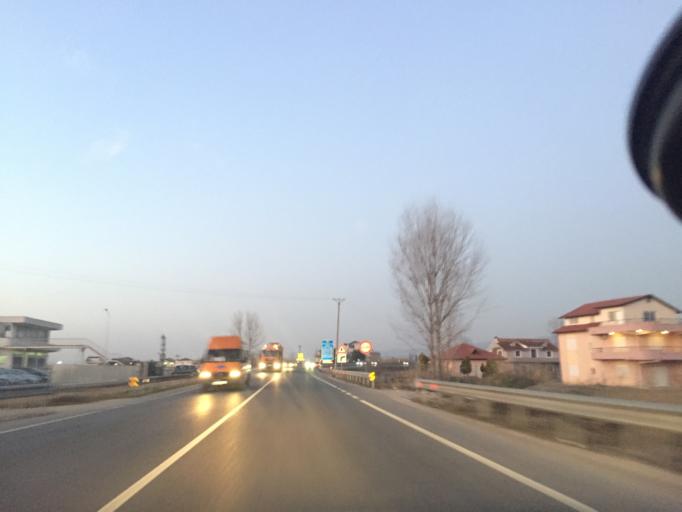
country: AL
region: Durres
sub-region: Rrethi i Krujes
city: Hasan
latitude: 41.4630
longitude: 19.6896
